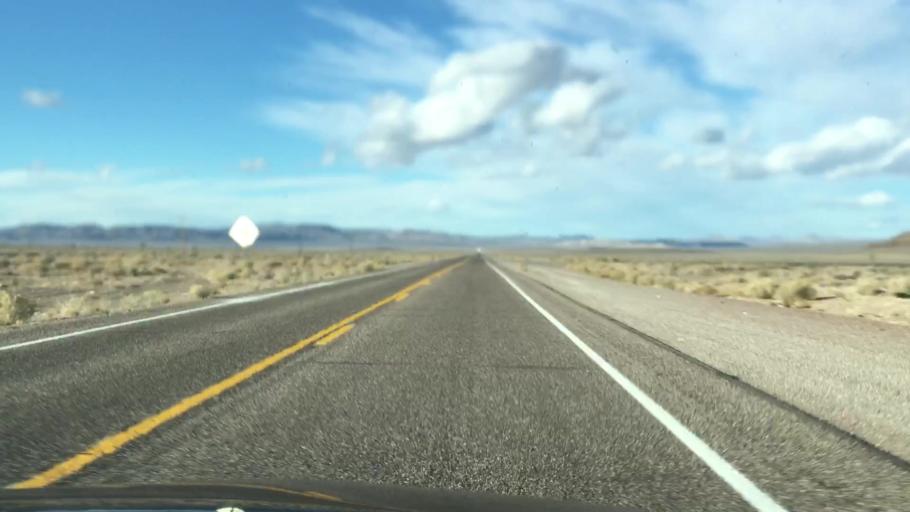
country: US
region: Nevada
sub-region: Esmeralda County
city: Goldfield
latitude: 37.3921
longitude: -117.1454
